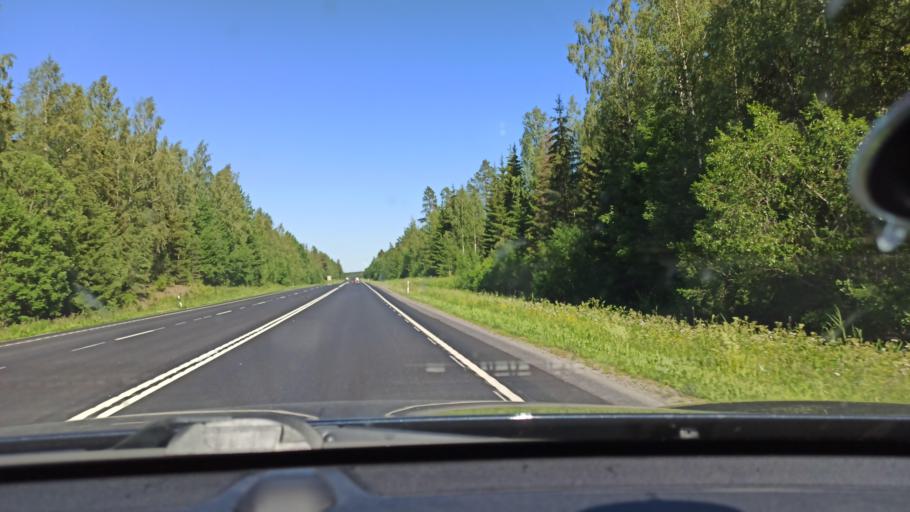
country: FI
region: Ostrobothnia
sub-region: Vaasa
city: Oravais
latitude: 63.2728
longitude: 22.3204
